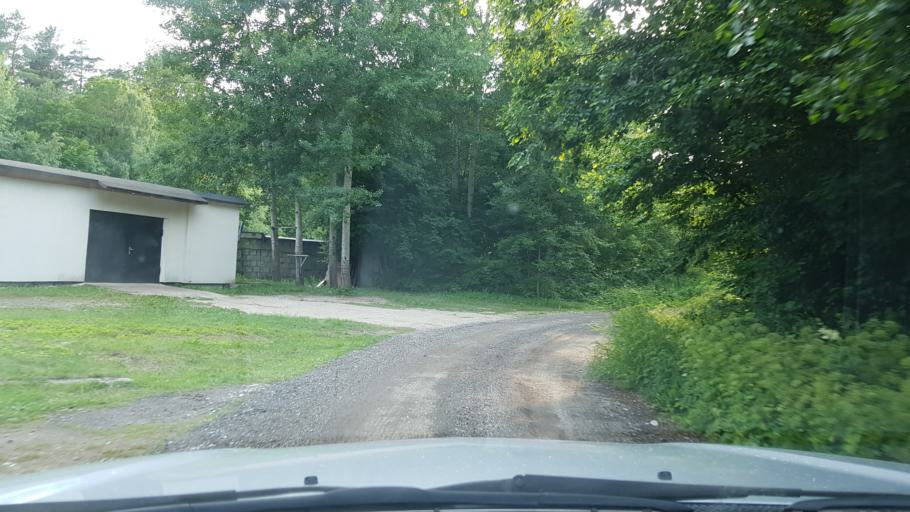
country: EE
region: Ida-Virumaa
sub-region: Narva-Joesuu linn
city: Narva-Joesuu
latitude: 59.4562
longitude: 28.0707
